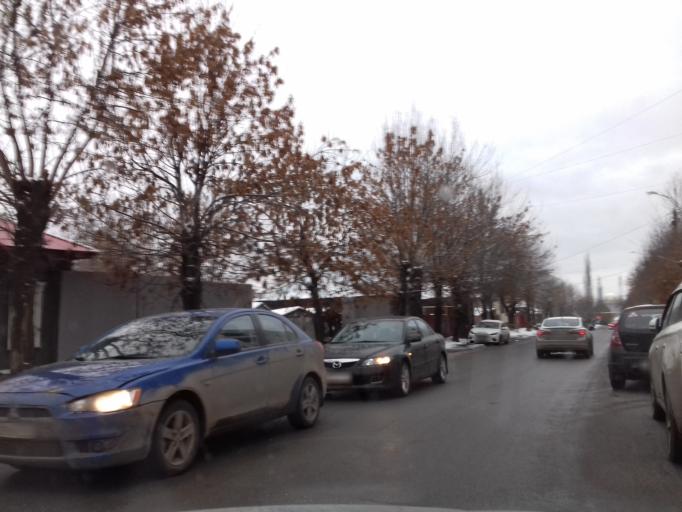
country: RU
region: Bashkortostan
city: Ufa
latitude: 54.7276
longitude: 55.9706
